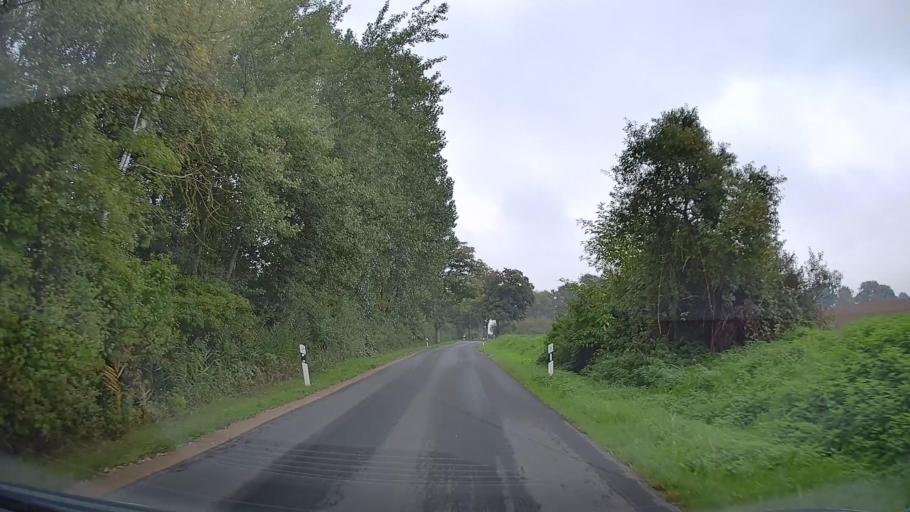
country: DE
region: Mecklenburg-Vorpommern
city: Hornstorf
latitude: 53.9011
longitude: 11.5098
